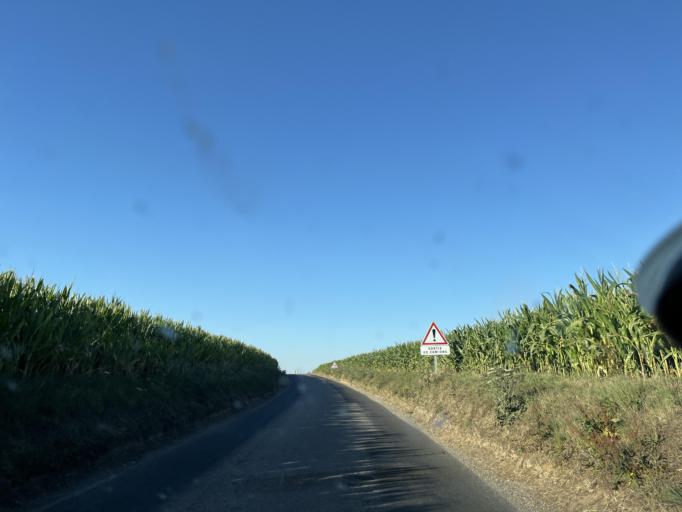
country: FR
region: Haute-Normandie
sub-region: Departement de la Seine-Maritime
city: Fauville-en-Caux
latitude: 49.6324
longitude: 0.6279
